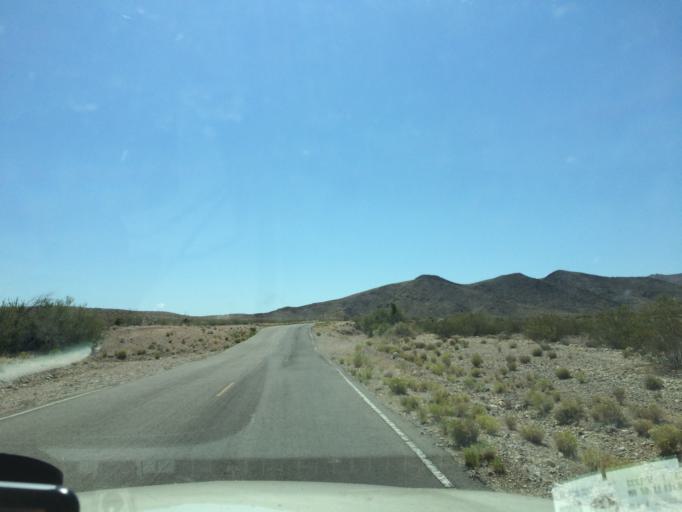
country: US
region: Nevada
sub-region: Clark County
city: Moapa Valley
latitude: 36.4472
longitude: -114.6739
